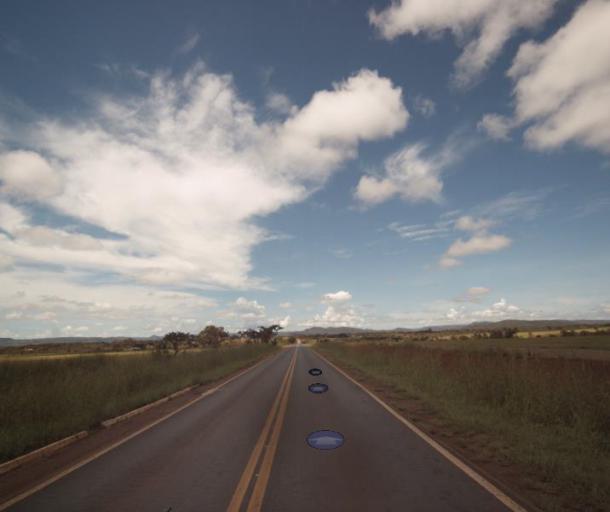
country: BR
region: Goias
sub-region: Padre Bernardo
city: Padre Bernardo
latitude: -15.3425
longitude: -48.2340
